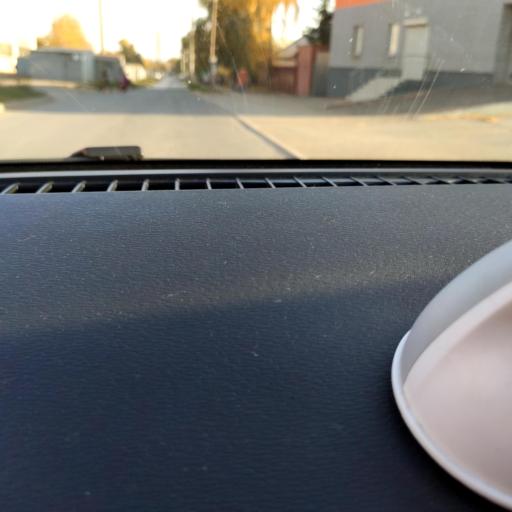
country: RU
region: Samara
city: Samara
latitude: 53.1931
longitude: 50.2192
